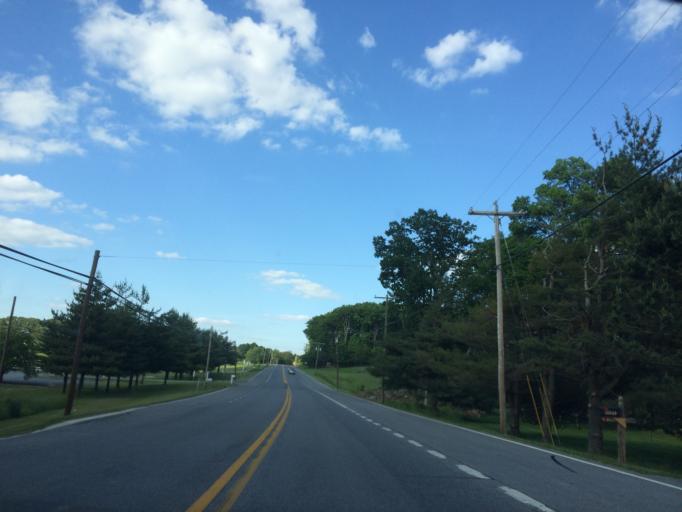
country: US
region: Maryland
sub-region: Frederick County
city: Walkersville
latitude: 39.4632
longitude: -77.2898
